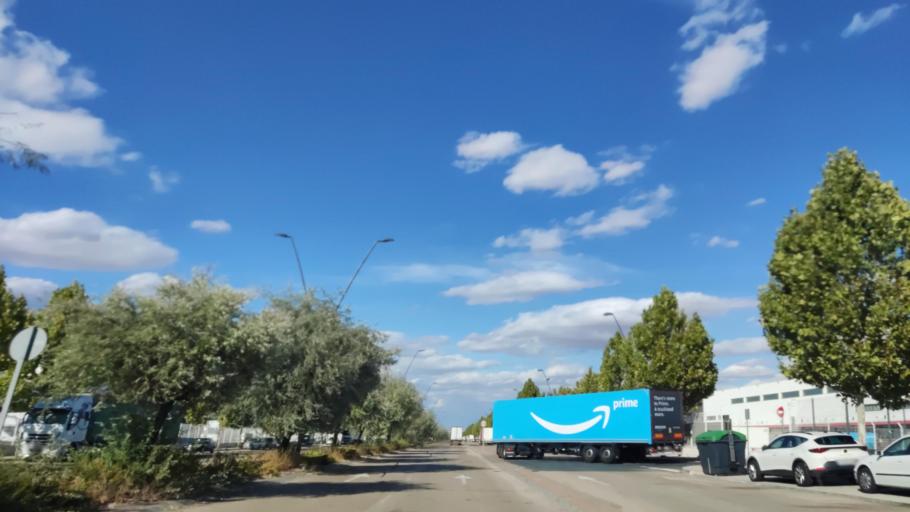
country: ES
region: Madrid
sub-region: Provincia de Madrid
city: Pinto
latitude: 40.2762
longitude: -3.6849
